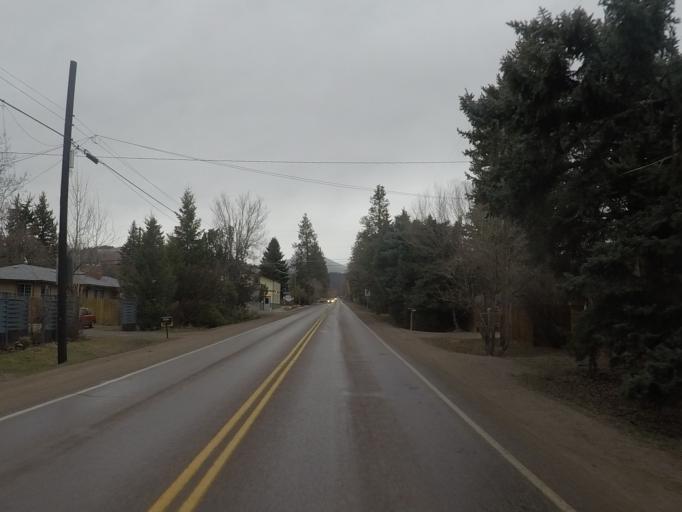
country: US
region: Montana
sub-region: Missoula County
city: East Missoula
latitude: 46.8864
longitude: -113.9657
